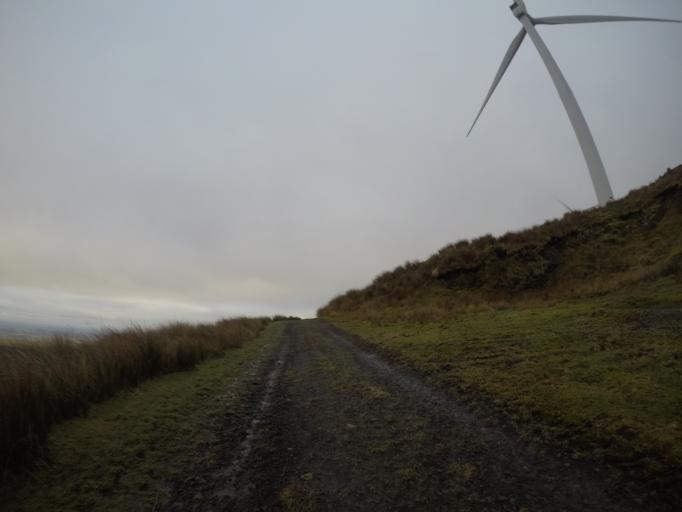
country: GB
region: Scotland
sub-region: North Ayrshire
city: Dalry
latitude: 55.7367
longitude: -4.7700
